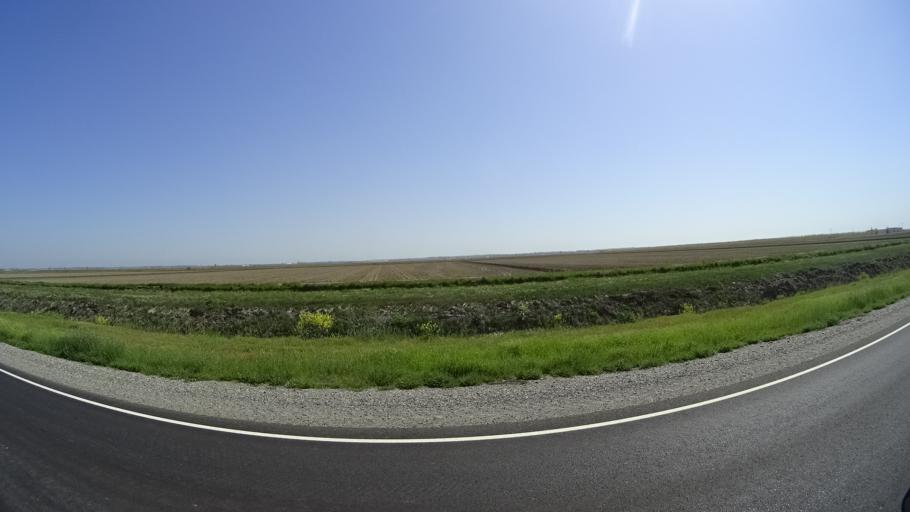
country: US
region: California
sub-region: Glenn County
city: Willows
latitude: 39.5264
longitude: -122.0653
